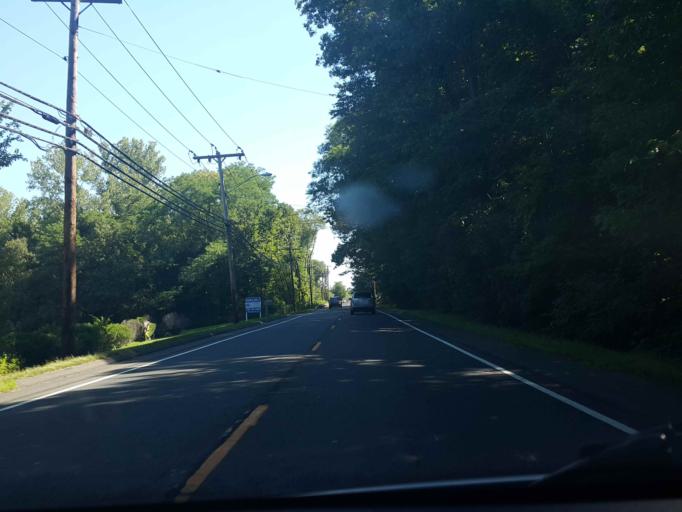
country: US
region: Connecticut
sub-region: New Haven County
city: North Branford
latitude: 41.3371
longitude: -72.7545
